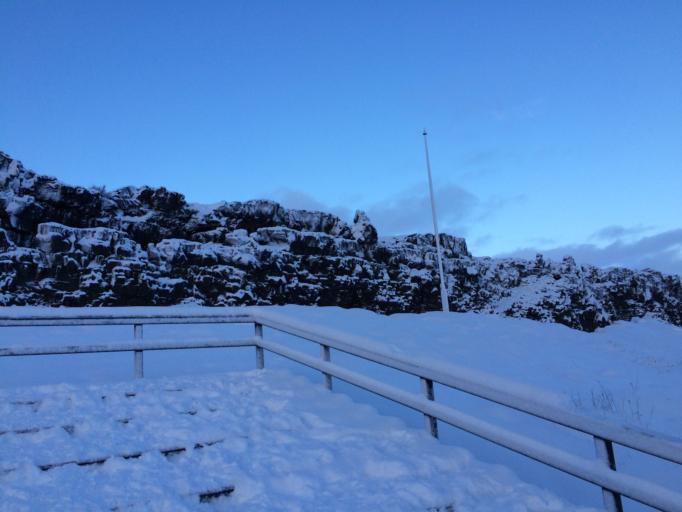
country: IS
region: South
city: Hveragerdi
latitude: 64.2594
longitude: -21.1225
